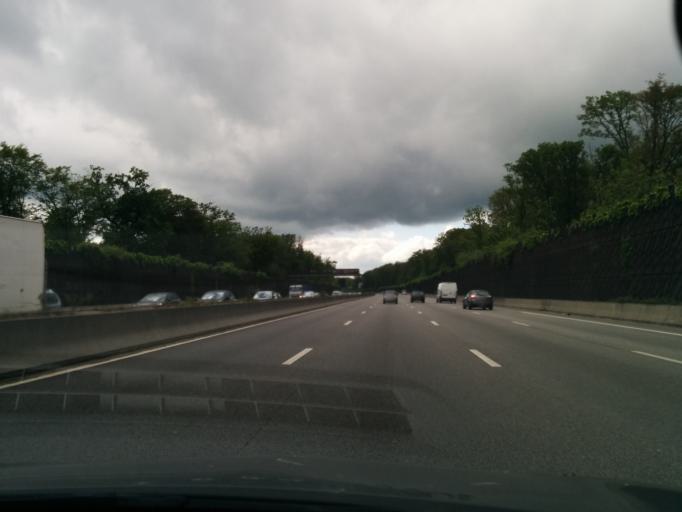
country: FR
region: Ile-de-France
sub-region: Departement des Yvelines
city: Le Chesnay
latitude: 48.8368
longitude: 2.1273
